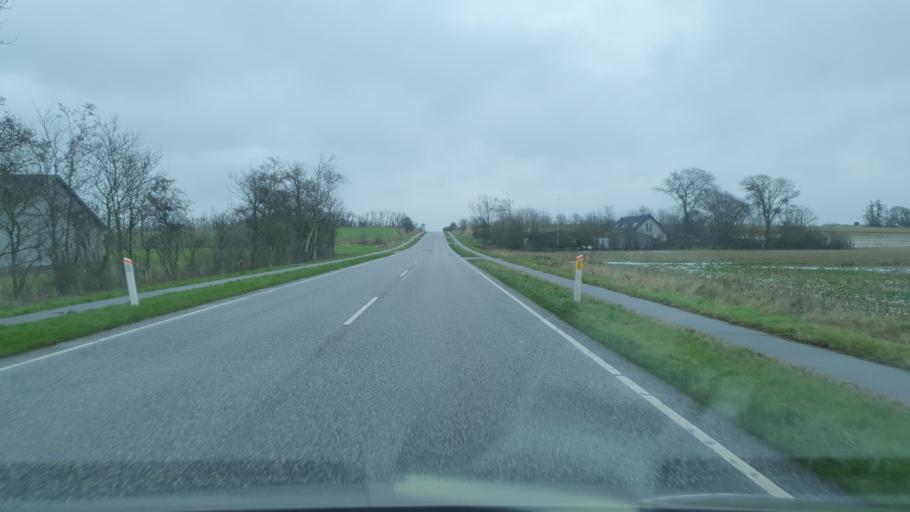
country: DK
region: North Denmark
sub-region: Jammerbugt Kommune
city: Fjerritslev
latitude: 57.0992
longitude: 9.1470
